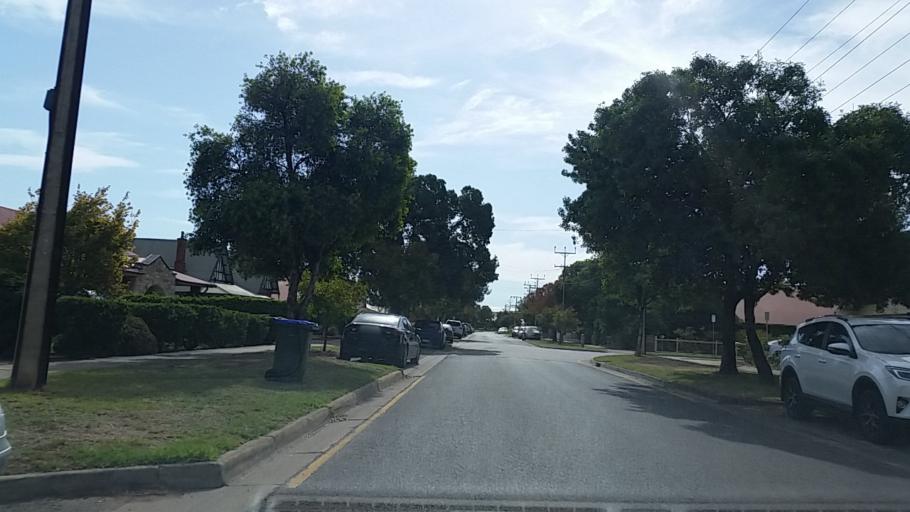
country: AU
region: South Australia
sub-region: Charles Sturt
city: Woodville North
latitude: -34.8786
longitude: 138.5363
